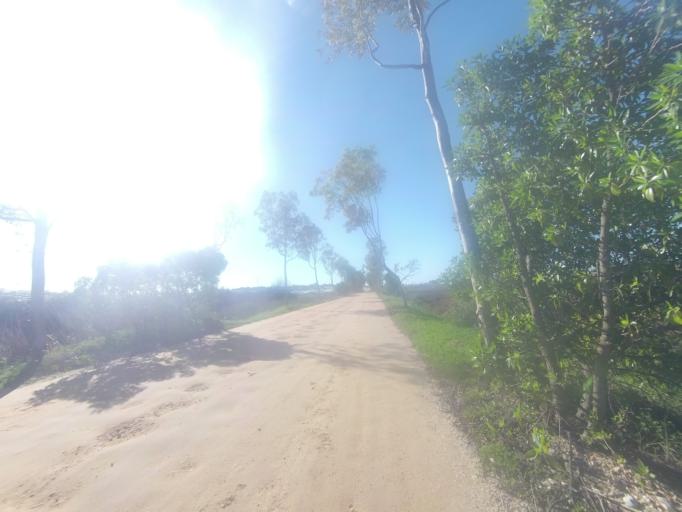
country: ES
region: Andalusia
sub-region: Provincia de Huelva
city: Palos de la Frontera
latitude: 37.2258
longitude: -6.9103
